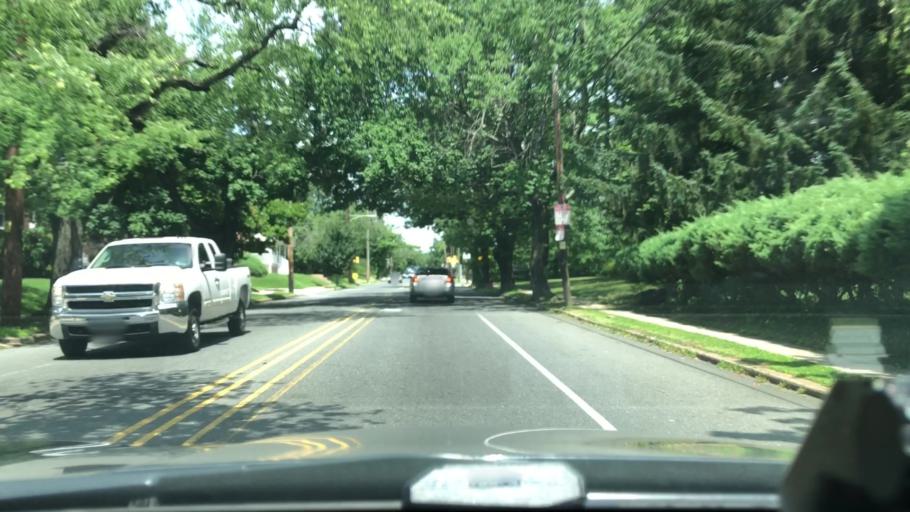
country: US
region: Pennsylvania
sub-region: Montgomery County
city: Wyndmoor
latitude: 40.0551
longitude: -75.1687
